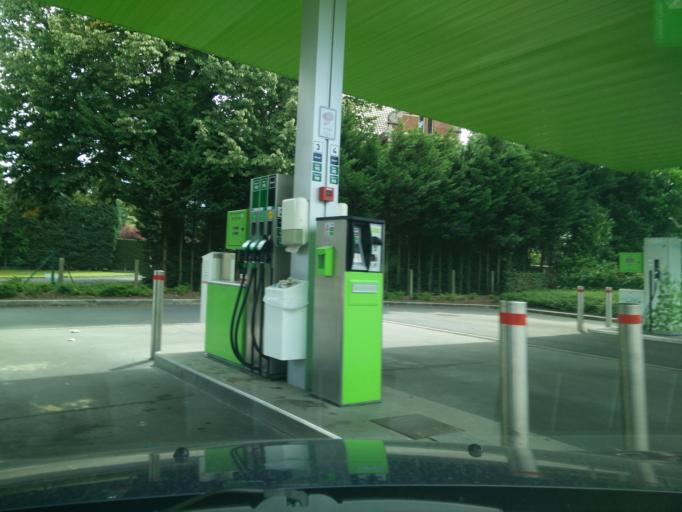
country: BE
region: Flanders
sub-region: Provincie Oost-Vlaanderen
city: Ledeberg
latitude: 51.0227
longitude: 3.7751
